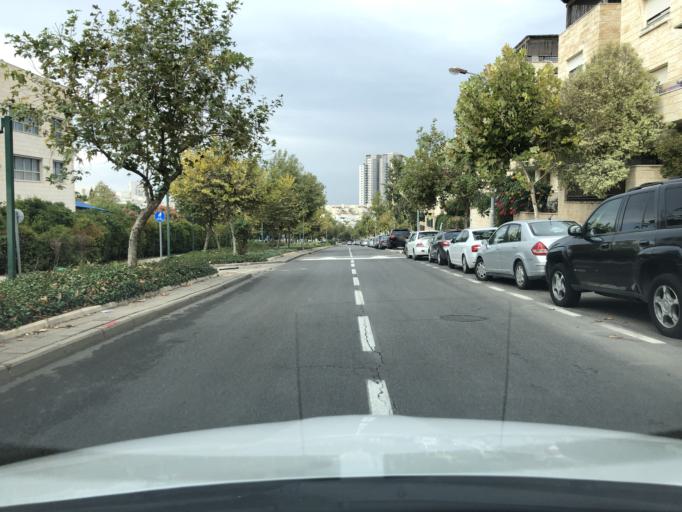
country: IL
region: Central District
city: Modiin
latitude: 31.9133
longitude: 35.0093
